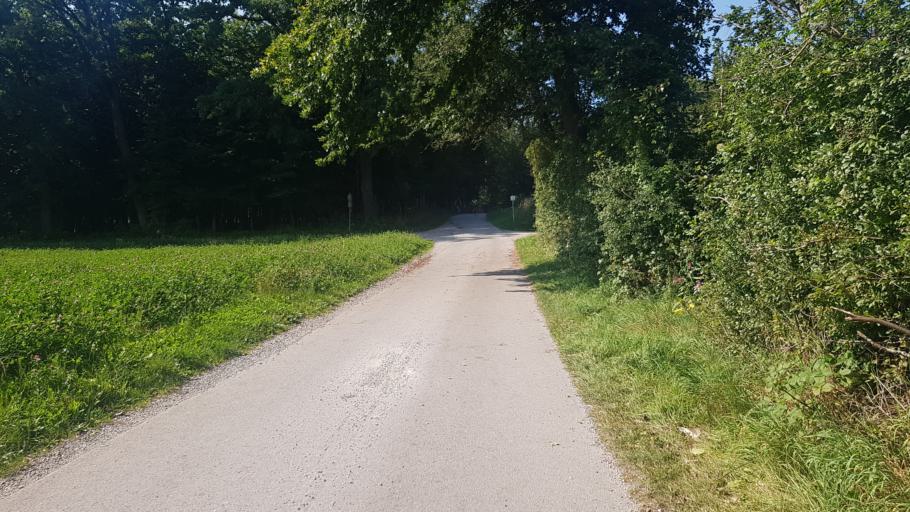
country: DE
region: Bavaria
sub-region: Upper Bavaria
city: Herrsching am Ammersee
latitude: 48.0251
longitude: 11.1562
